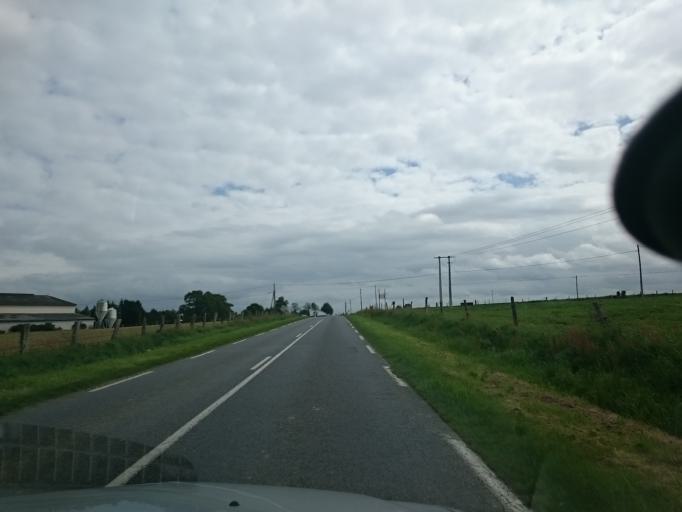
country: FR
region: Lower Normandy
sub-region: Departement de la Manche
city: Pontorson
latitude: 48.5118
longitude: -1.4780
